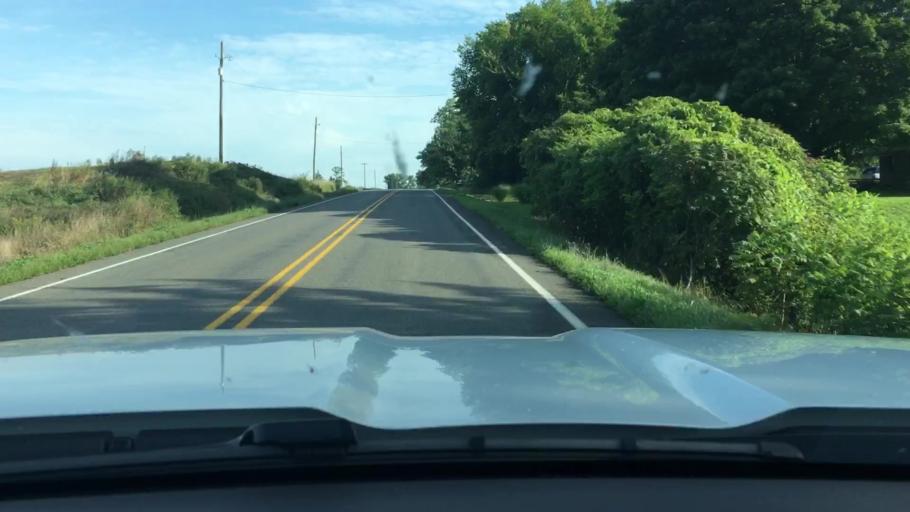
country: US
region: Michigan
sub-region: Kent County
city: Kent City
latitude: 43.1955
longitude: -85.7707
